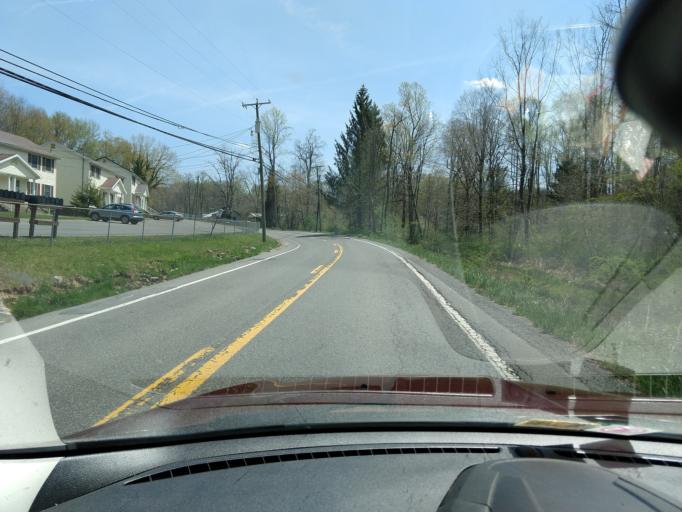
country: US
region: West Virginia
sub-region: Raleigh County
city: Bradley
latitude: 37.8537
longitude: -81.2057
